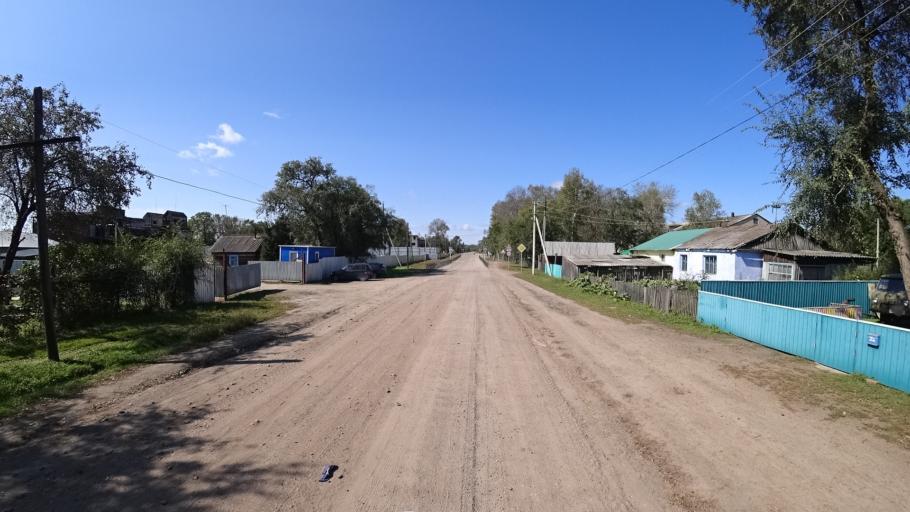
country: RU
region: Amur
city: Arkhara
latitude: 49.4027
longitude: 130.1416
